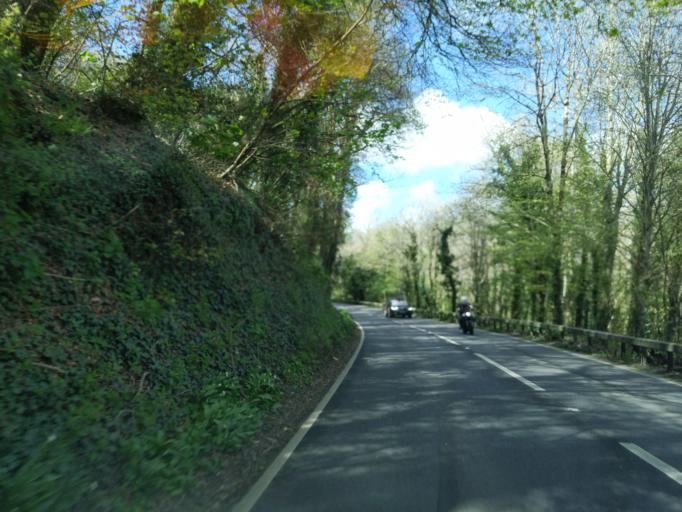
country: GB
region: England
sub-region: Cornwall
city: Wadebridge
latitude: 50.5066
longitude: -4.7814
